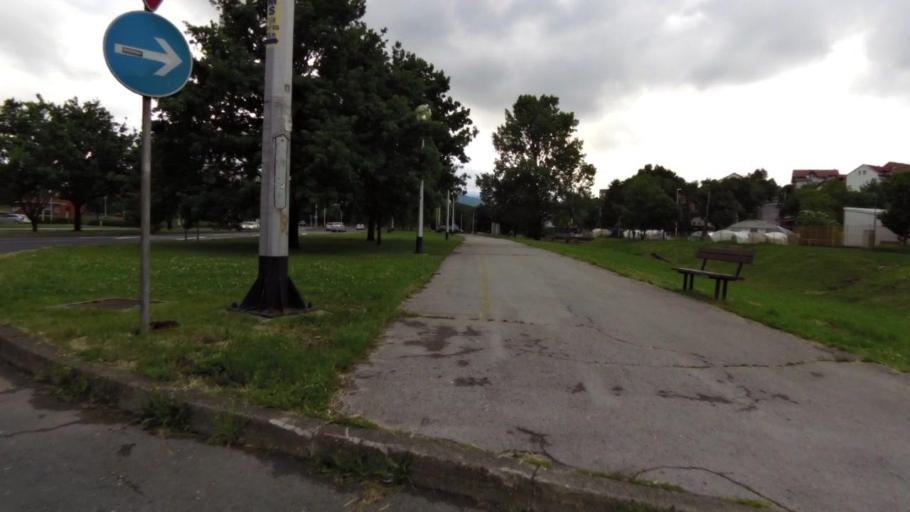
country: HR
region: Grad Zagreb
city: Dubrava
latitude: 45.8379
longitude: 16.0330
